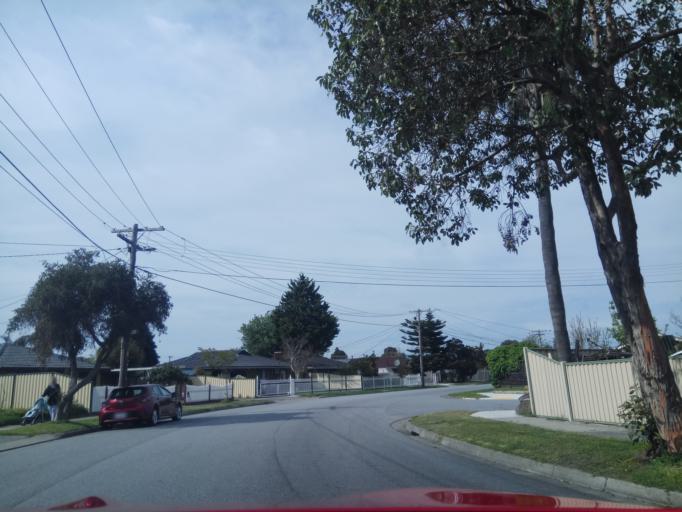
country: AU
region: Victoria
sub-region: Greater Dandenong
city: Springvale South
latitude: -37.9755
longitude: 145.1488
